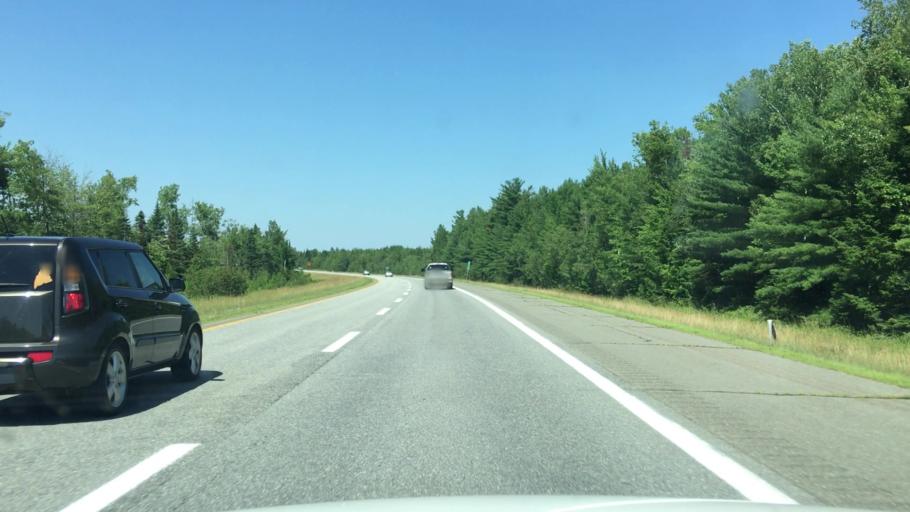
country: US
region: Maine
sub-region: Penobscot County
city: Howland
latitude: 45.2117
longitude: -68.6769
